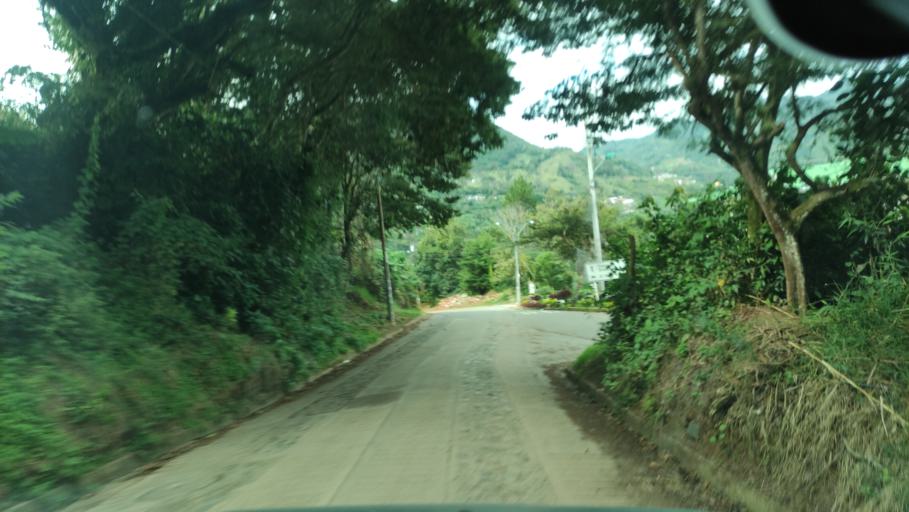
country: CO
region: Valle del Cauca
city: Cali
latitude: 3.4541
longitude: -76.6345
